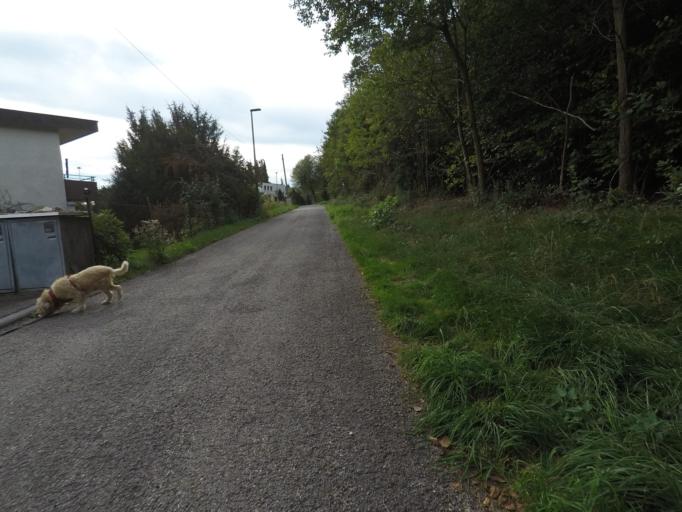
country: DE
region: Baden-Wuerttemberg
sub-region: Regierungsbezirk Stuttgart
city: Steinenbronn
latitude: 48.7260
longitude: 9.0905
